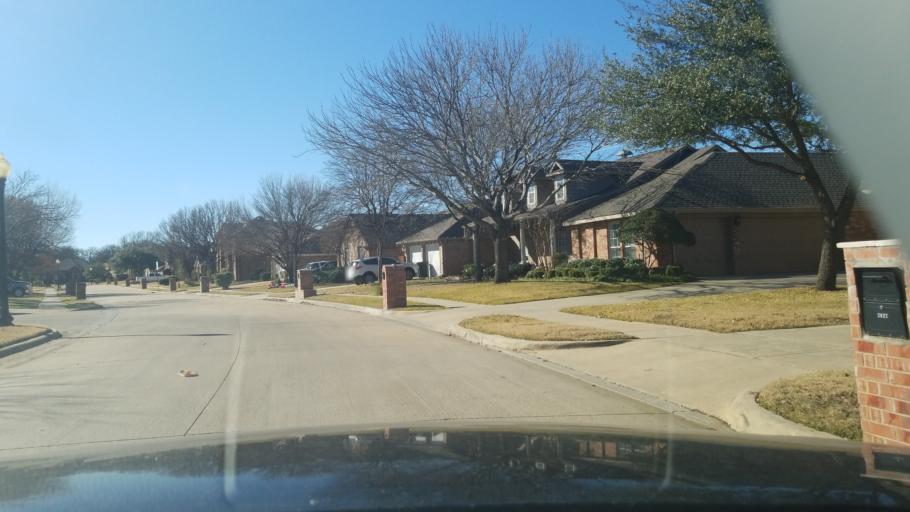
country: US
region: Texas
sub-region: Denton County
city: Corinth
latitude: 33.1632
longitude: -97.0804
